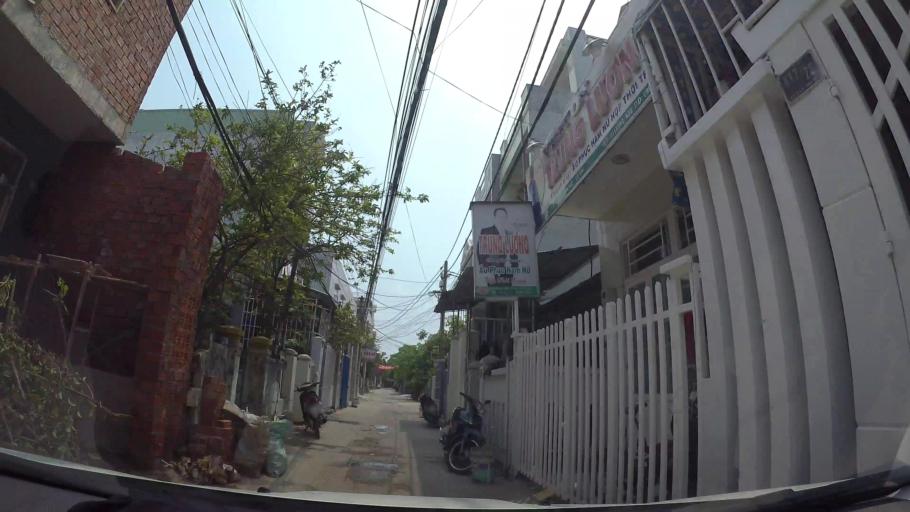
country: VN
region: Da Nang
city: Son Tra
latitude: 16.0995
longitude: 108.2496
